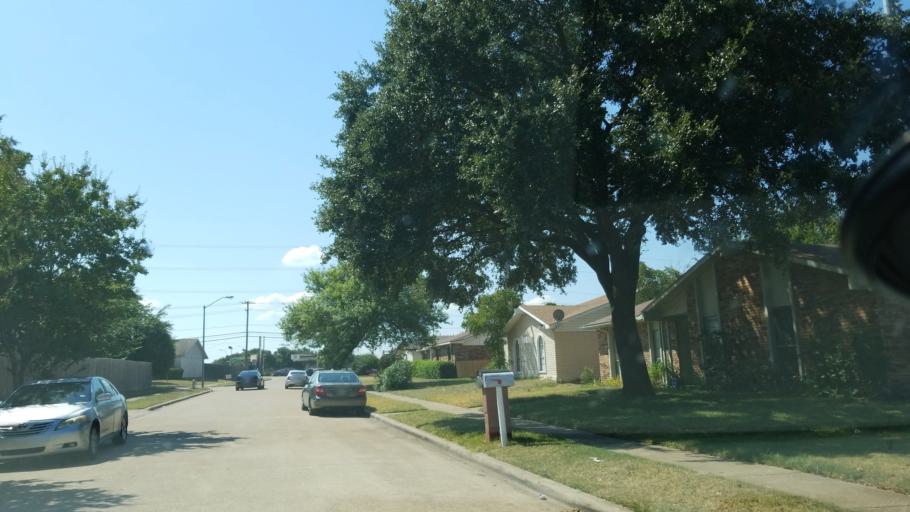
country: US
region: Texas
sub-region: Dallas County
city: Richardson
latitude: 32.9103
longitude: -96.7080
